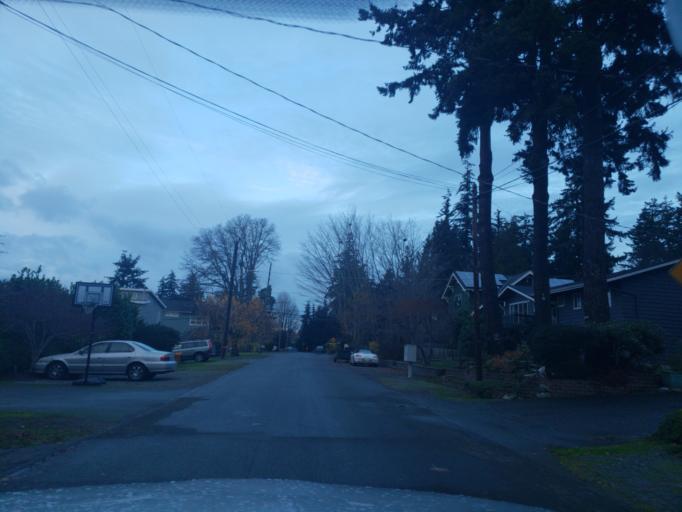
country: US
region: Washington
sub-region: Snohomish County
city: Woodway
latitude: 47.7698
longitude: -122.3853
